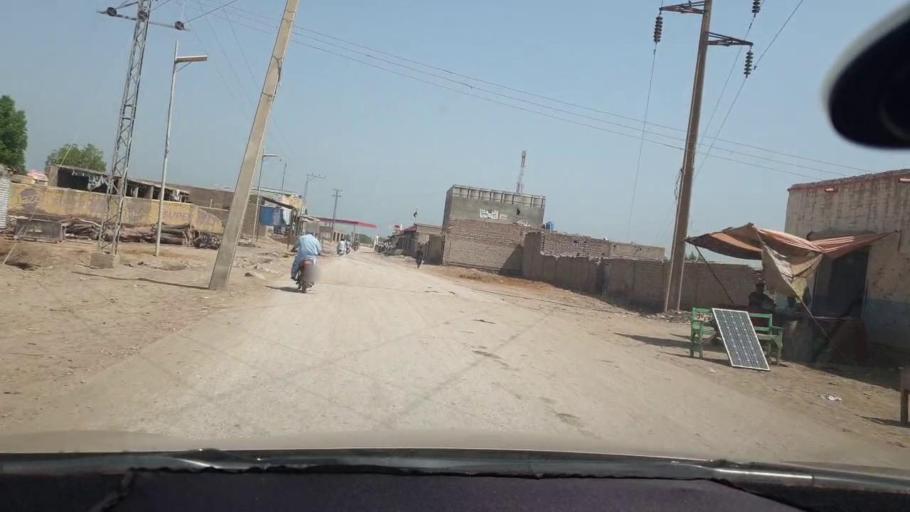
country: PK
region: Sindh
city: Kambar
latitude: 27.5906
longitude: 67.9922
